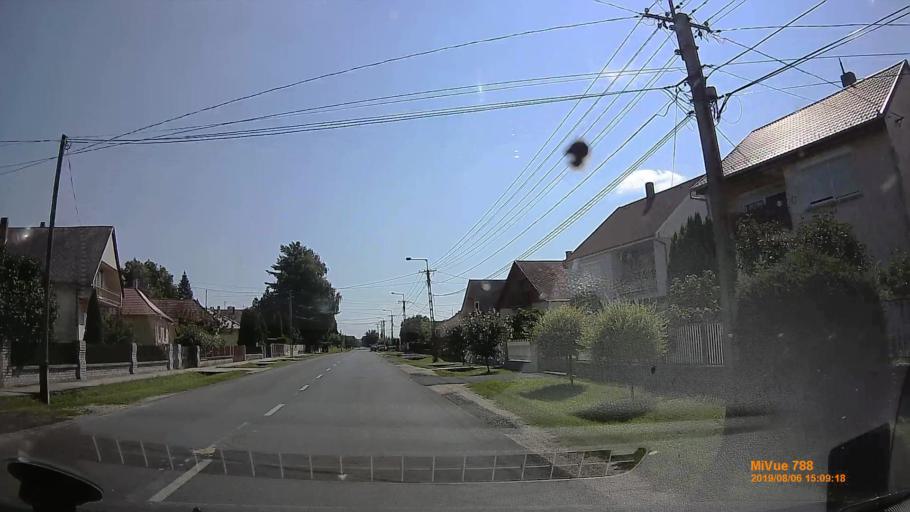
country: HU
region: Zala
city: Nagykanizsa
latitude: 46.4056
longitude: 16.9835
